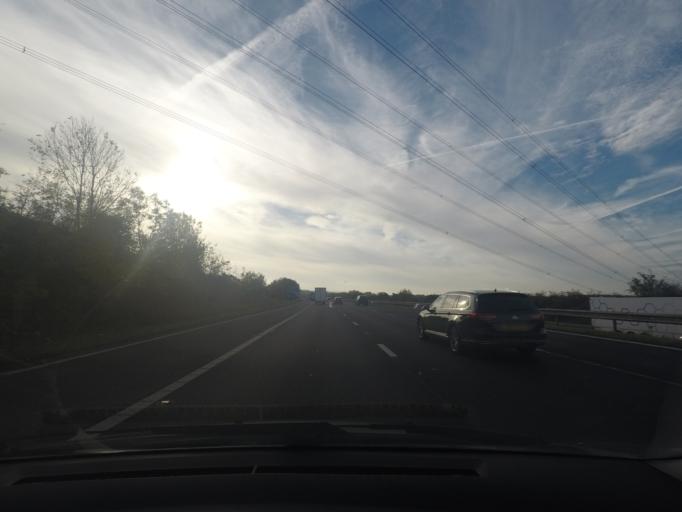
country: GB
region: England
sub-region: Barnsley
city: Darton
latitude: 53.5666
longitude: -1.5399
